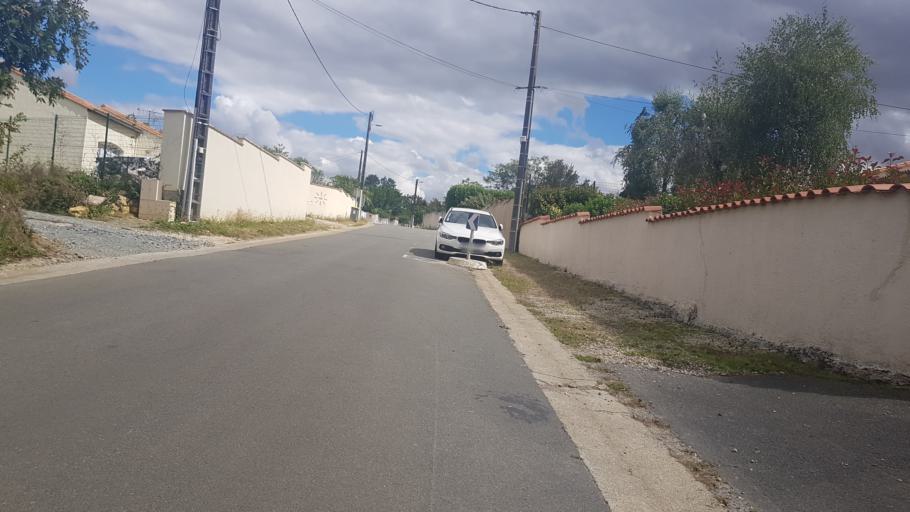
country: FR
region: Poitou-Charentes
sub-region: Departement des Deux-Sevres
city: Vouille
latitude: 46.3308
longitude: -0.3634
